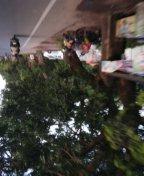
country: IN
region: Kerala
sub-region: Thrissur District
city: Trichur
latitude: 10.5405
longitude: 76.1846
